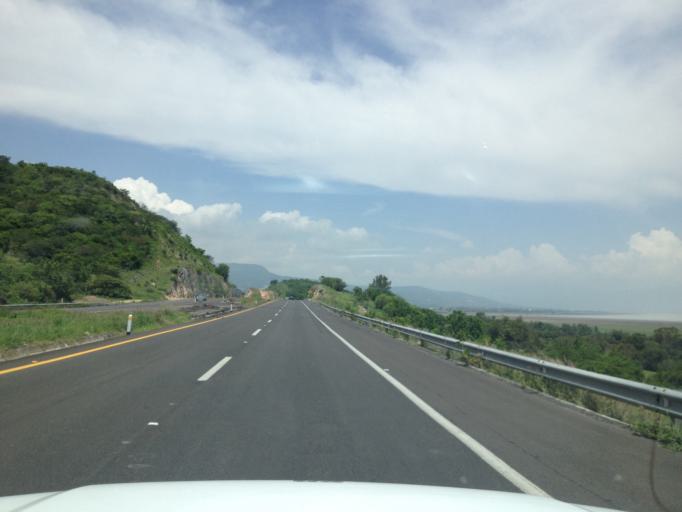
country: MX
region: Michoacan
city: Copandaro de Galeana
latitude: 19.8920
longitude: -101.1678
